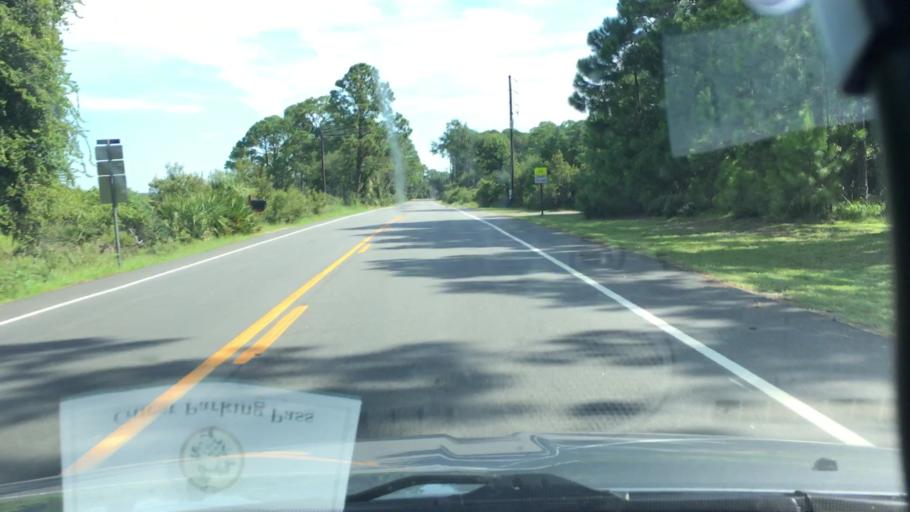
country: US
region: South Carolina
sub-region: Beaufort County
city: Beaufort
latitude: 32.3807
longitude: -80.4438
